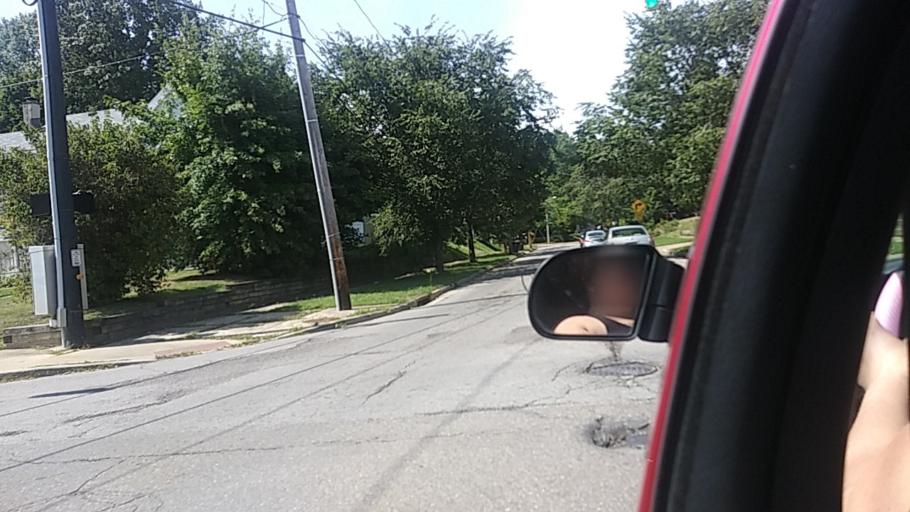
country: US
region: Ohio
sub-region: Summit County
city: Akron
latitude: 41.0788
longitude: -81.5487
